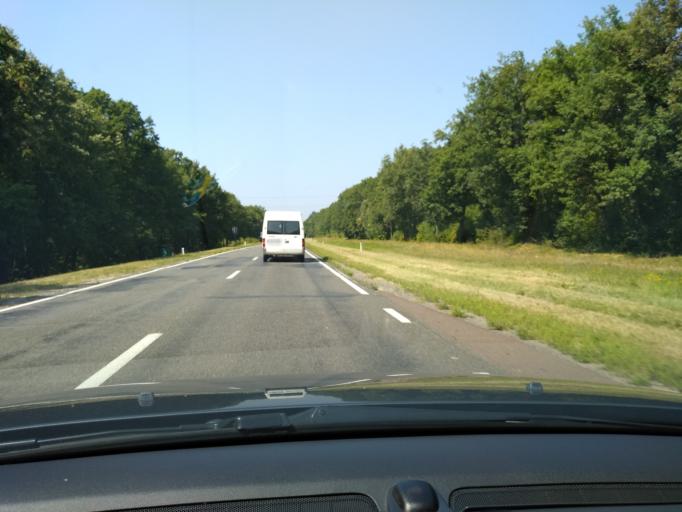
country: MD
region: Straseni
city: Straseni
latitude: 47.0376
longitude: 28.5894
